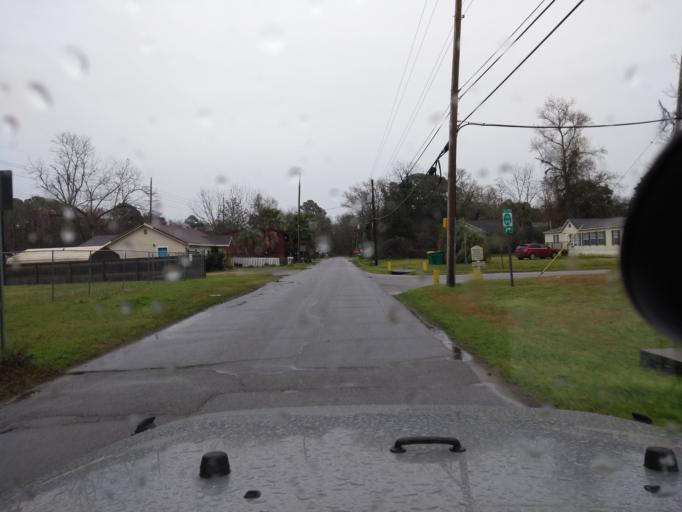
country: US
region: Georgia
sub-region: Chatham County
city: Garden City
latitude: 32.0913
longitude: -81.1590
